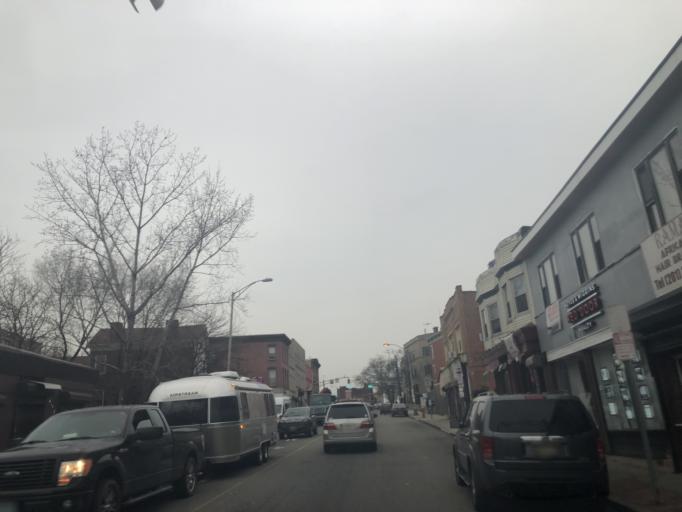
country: US
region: New Jersey
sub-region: Hudson County
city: Jersey City
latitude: 40.7156
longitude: -74.0683
